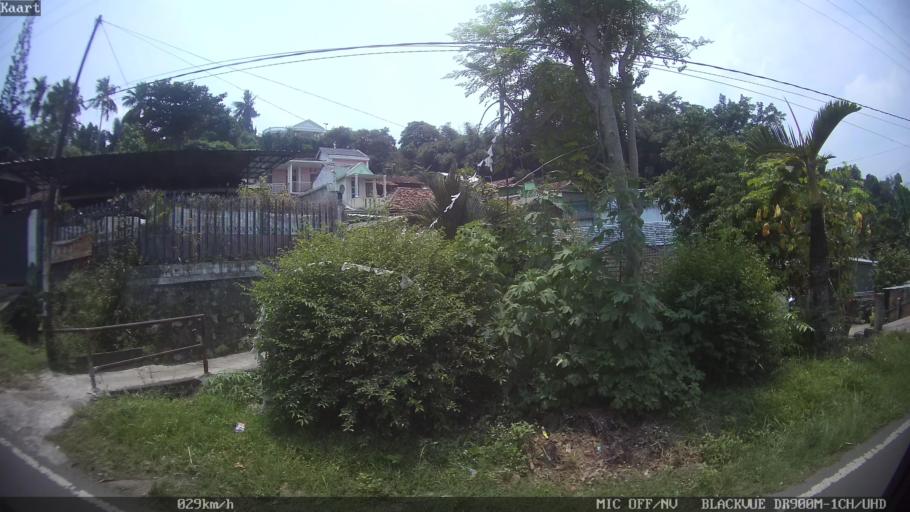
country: ID
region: Lampung
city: Bandarlampung
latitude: -5.4327
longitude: 105.2728
